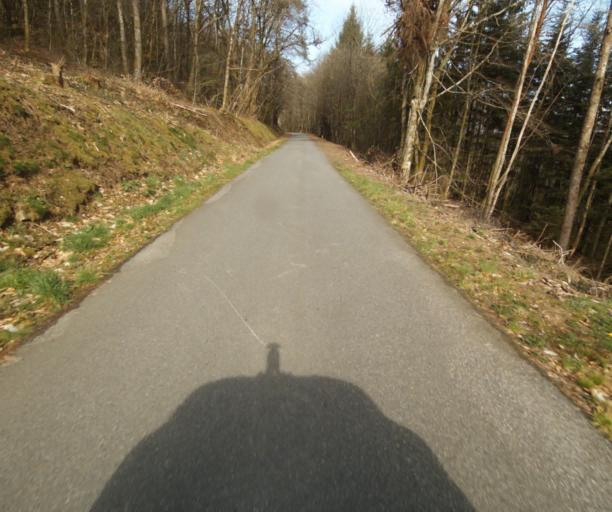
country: FR
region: Limousin
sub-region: Departement de la Correze
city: Correze
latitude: 45.3424
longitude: 1.8512
